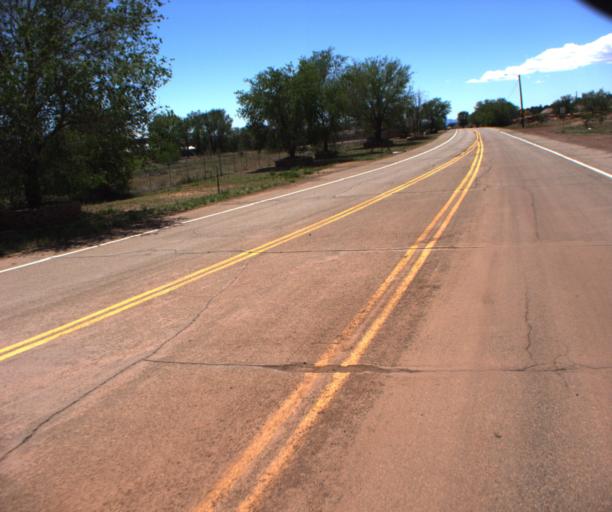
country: US
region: Arizona
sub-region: Coconino County
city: Williams
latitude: 35.2246
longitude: -112.4909
